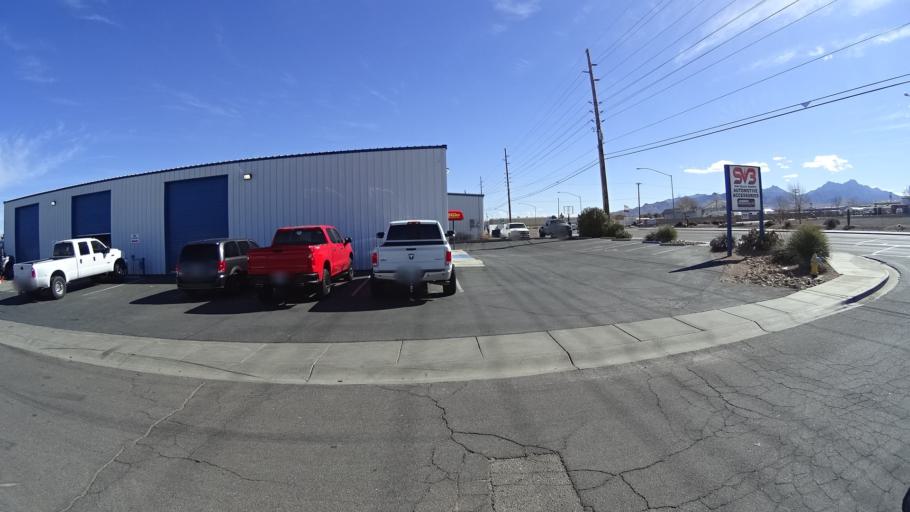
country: US
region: Arizona
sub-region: Mohave County
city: New Kingman-Butler
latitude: 35.2252
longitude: -114.0191
